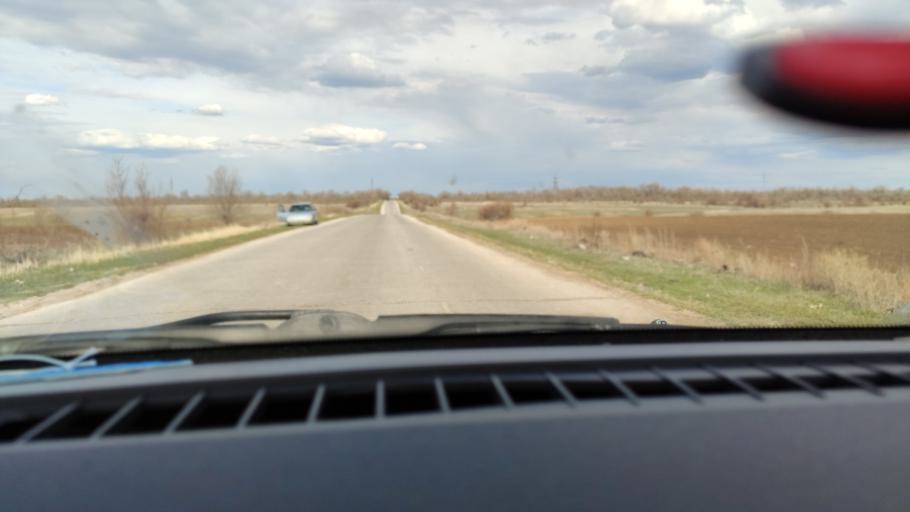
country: RU
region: Saratov
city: Rovnoye
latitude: 50.9412
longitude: 46.1259
